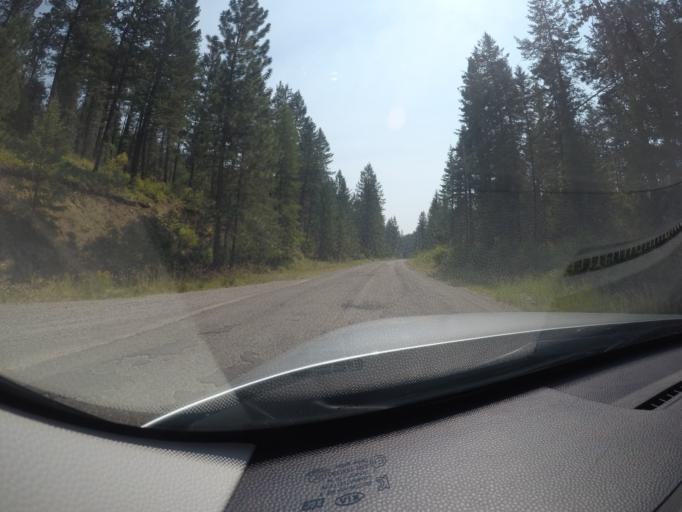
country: US
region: Montana
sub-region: Lake County
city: Polson
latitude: 47.7787
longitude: -114.1723
